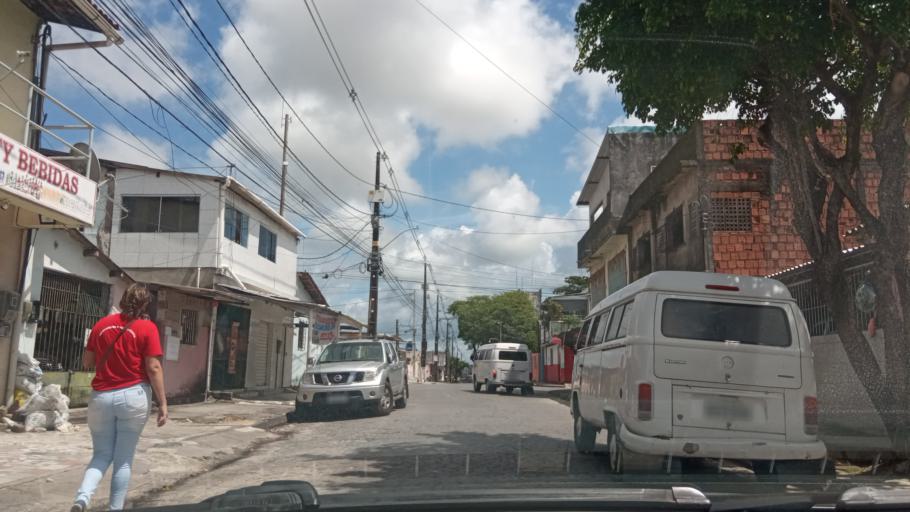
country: BR
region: Pernambuco
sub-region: Jaboatao Dos Guararapes
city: Jaboatao dos Guararapes
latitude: -8.1189
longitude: -34.9455
